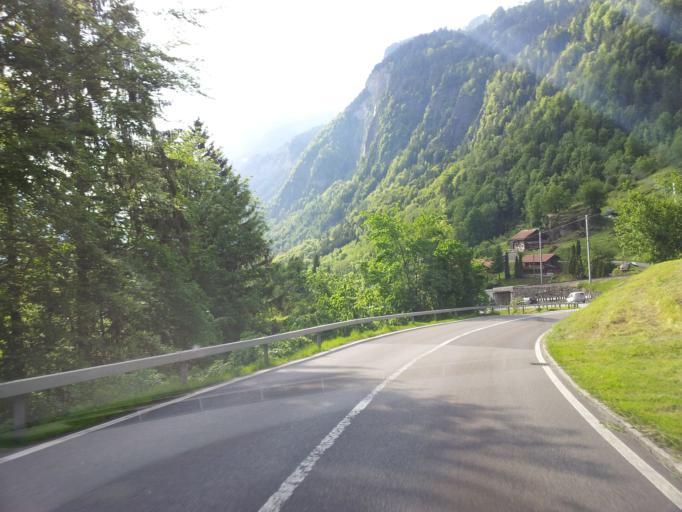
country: CH
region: Bern
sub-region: Interlaken-Oberhasli District
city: Grindelwald
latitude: 46.6365
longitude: 7.9692
